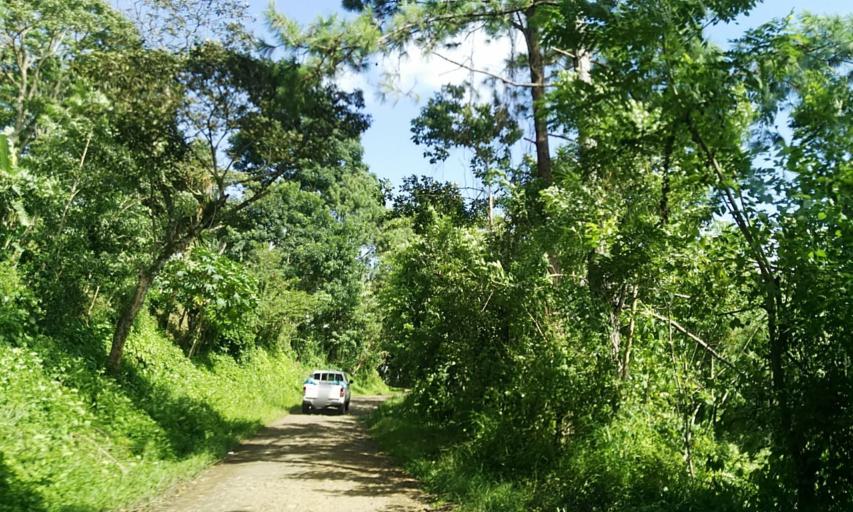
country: NI
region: Matagalpa
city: San Ramon
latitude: 12.9907
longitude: -85.8558
